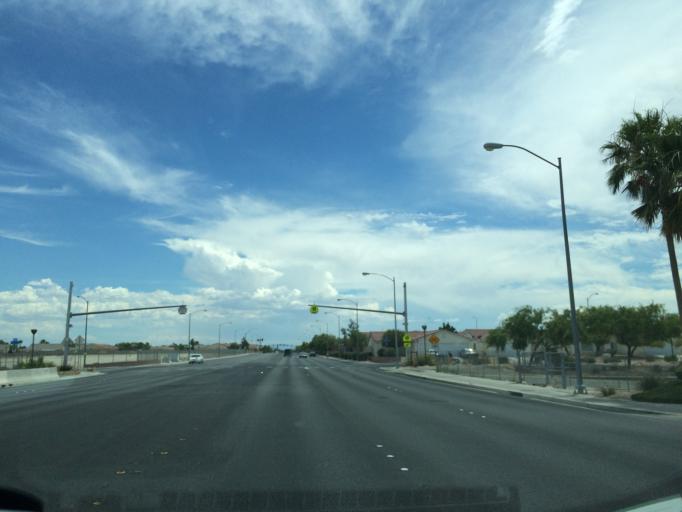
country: US
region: Nevada
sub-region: Clark County
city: North Las Vegas
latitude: 36.2588
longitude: -115.1800
